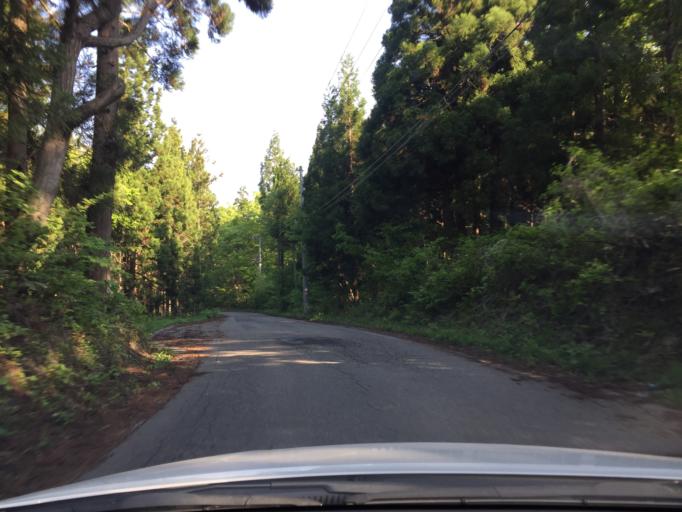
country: JP
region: Fukushima
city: Kitakata
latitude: 37.6746
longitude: 139.8057
